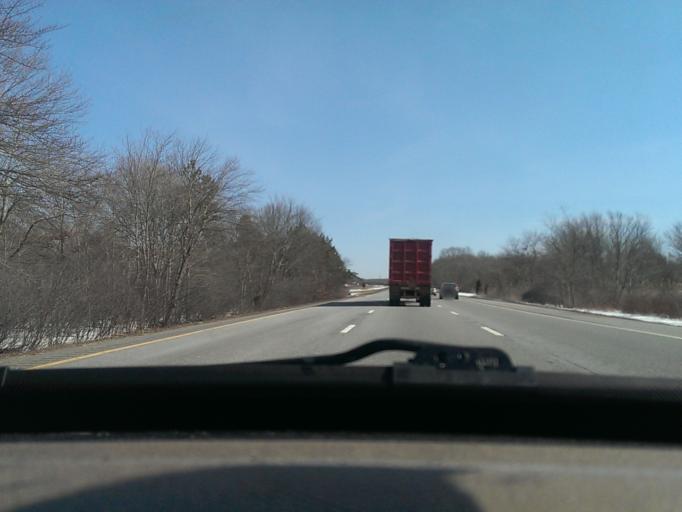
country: US
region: Massachusetts
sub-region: Bristol County
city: Seekonk
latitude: 41.7862
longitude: -71.2973
